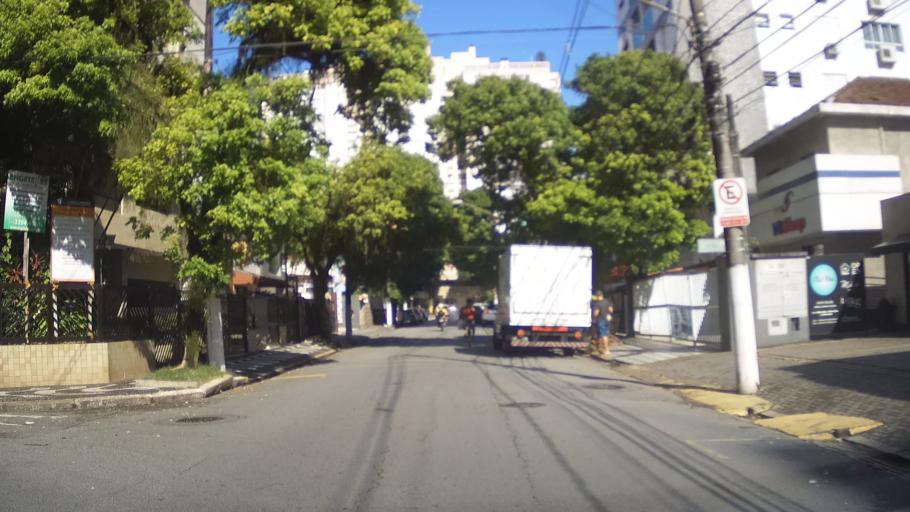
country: BR
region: Sao Paulo
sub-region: Santos
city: Santos
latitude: -23.9646
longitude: -46.3269
